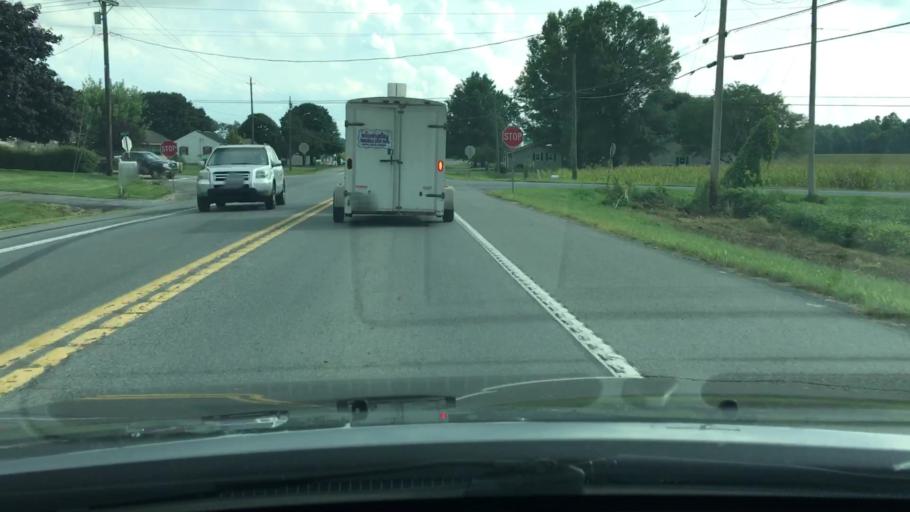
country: US
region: Pennsylvania
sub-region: Franklin County
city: Scotland
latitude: 39.9453
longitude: -77.5833
